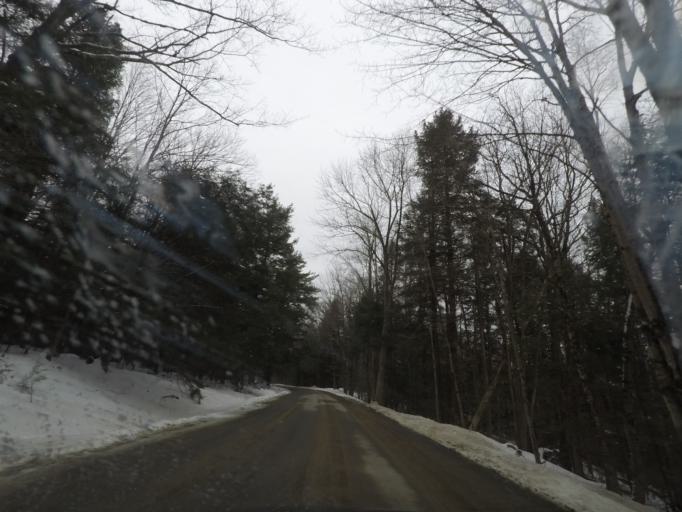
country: US
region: New York
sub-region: Rensselaer County
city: Averill Park
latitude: 42.5485
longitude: -73.4133
